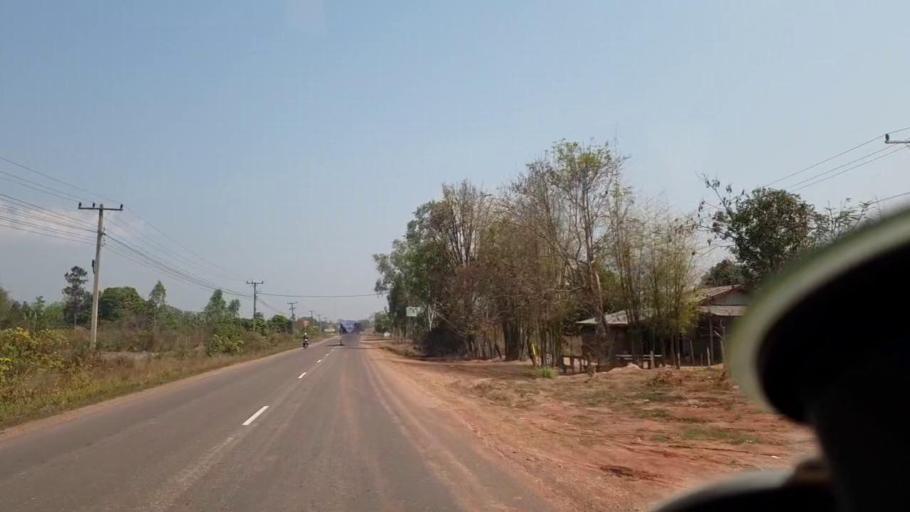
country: TH
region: Nong Khai
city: Phon Phisai
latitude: 18.1152
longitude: 103.0280
